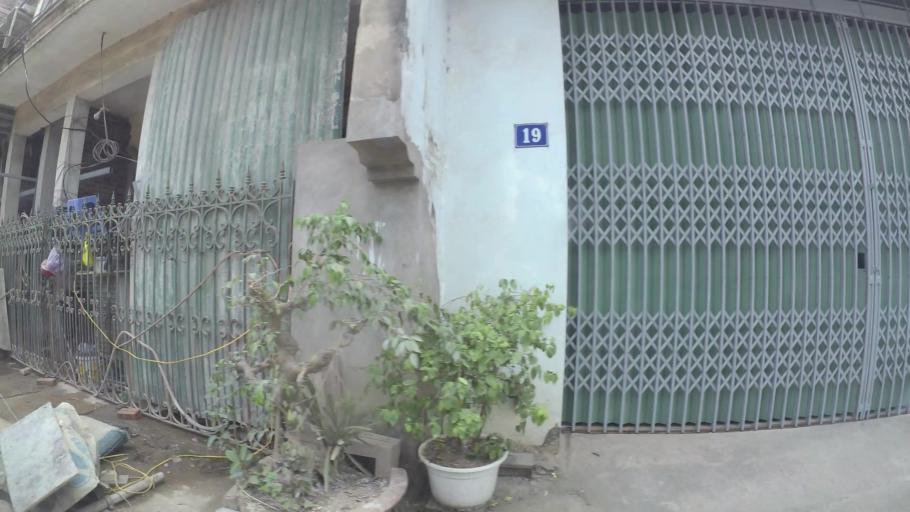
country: VN
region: Ha Noi
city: Ha Dong
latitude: 20.9907
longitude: 105.7372
